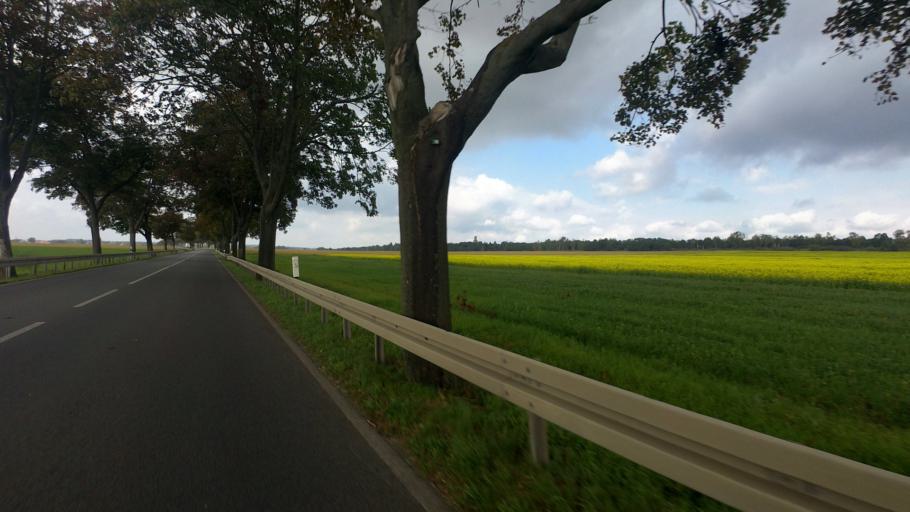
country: DE
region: Brandenburg
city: Plessa
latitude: 51.4678
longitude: 13.5918
